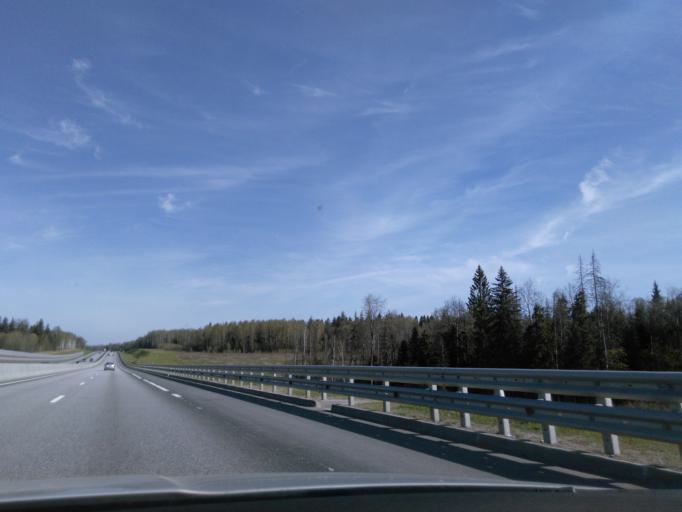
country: RU
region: Moskovskaya
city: Lozhki
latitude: 56.1213
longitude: 37.1140
